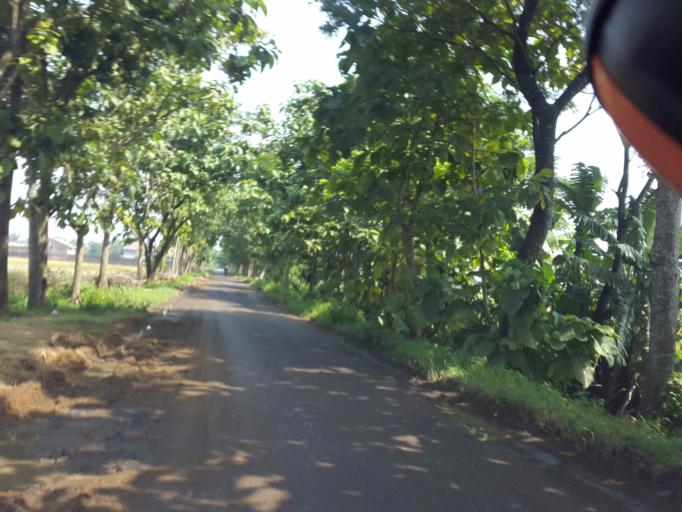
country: ID
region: Central Java
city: Sragen
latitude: -7.4361
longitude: 110.9499
